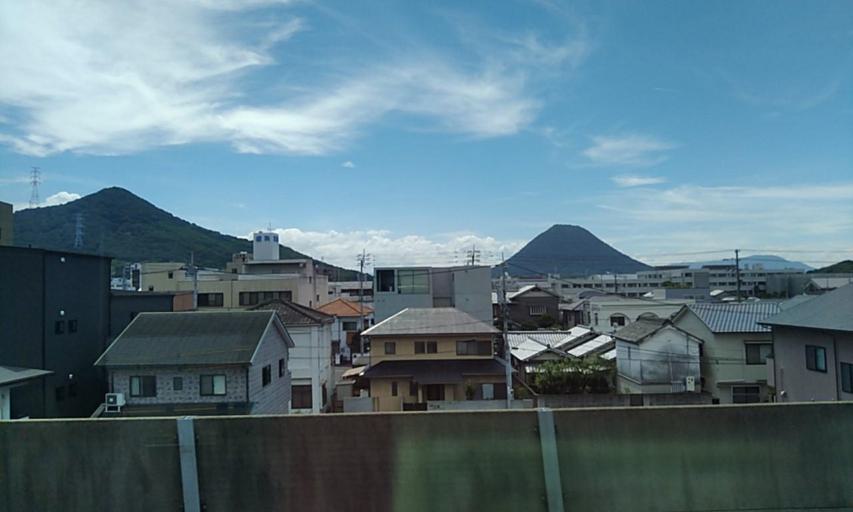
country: JP
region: Kagawa
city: Sakaidecho
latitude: 34.3131
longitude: 133.8541
